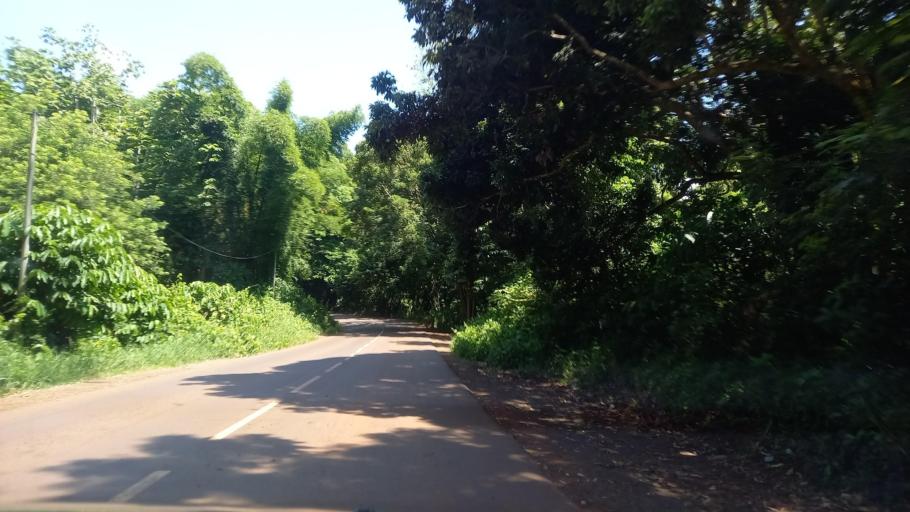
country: YT
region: Ouangani
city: Ouangani
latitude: -12.8339
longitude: 45.1388
